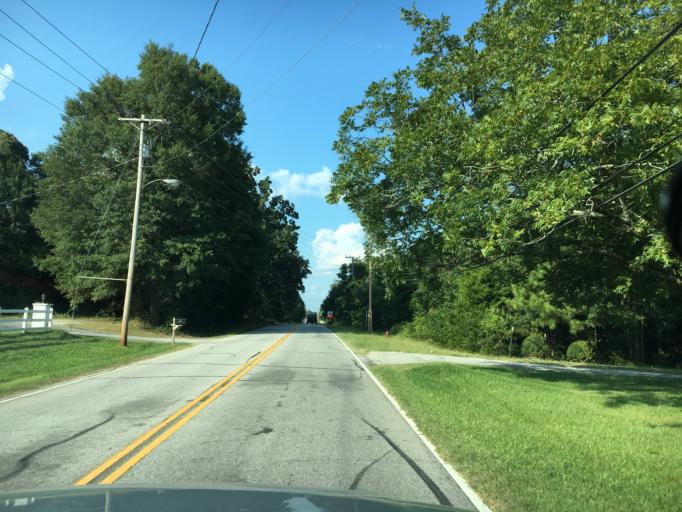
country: US
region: South Carolina
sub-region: Laurens County
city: Clinton
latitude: 34.4850
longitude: -81.8728
